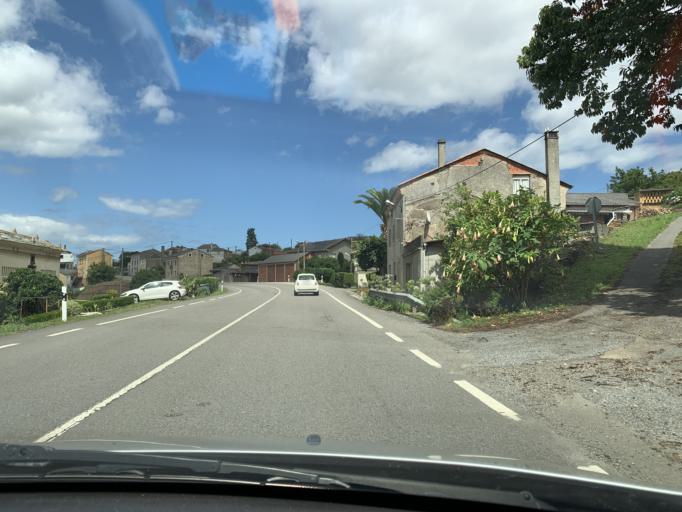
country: ES
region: Galicia
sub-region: Provincia de Lugo
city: Barreiros
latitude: 43.5165
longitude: -7.2714
